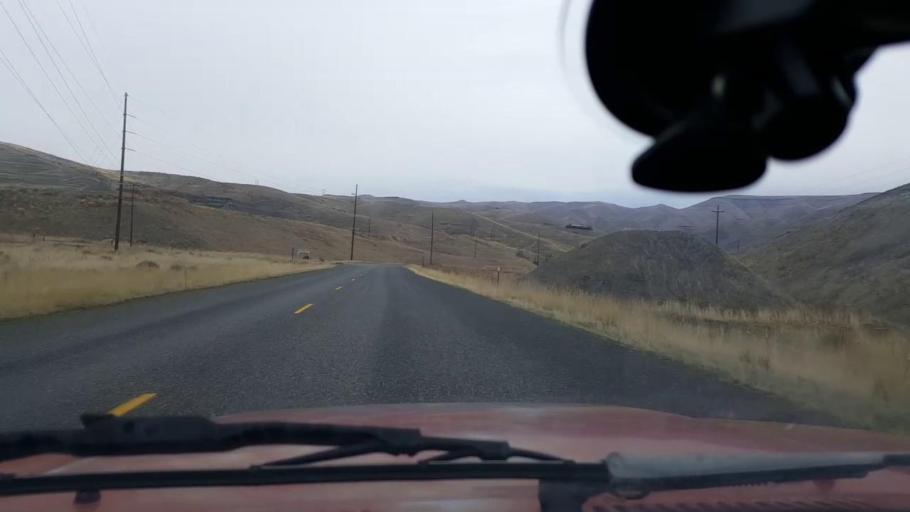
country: US
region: Washington
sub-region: Asotin County
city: Clarkston Heights-Vineland
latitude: 46.4078
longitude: -117.1071
